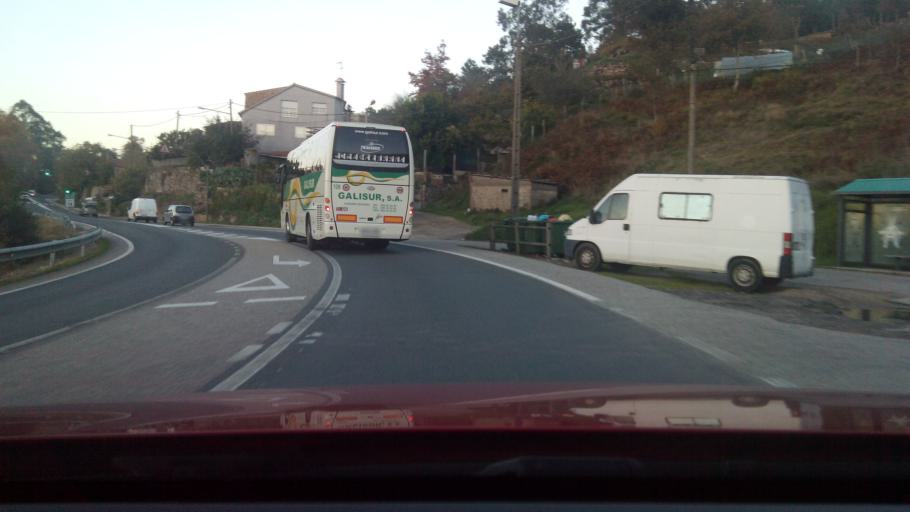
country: ES
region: Galicia
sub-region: Provincia de Pontevedra
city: Gondomar
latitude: 42.1491
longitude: -8.7261
